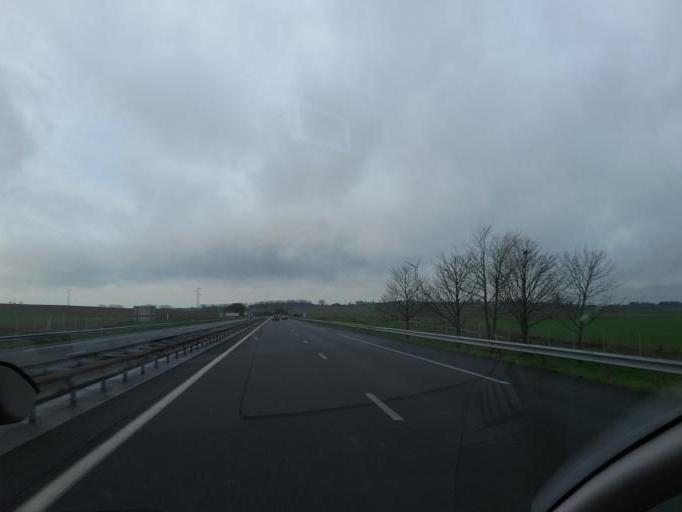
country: FR
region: Picardie
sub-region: Departement de la Somme
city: Moislains
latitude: 50.0382
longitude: 2.9105
